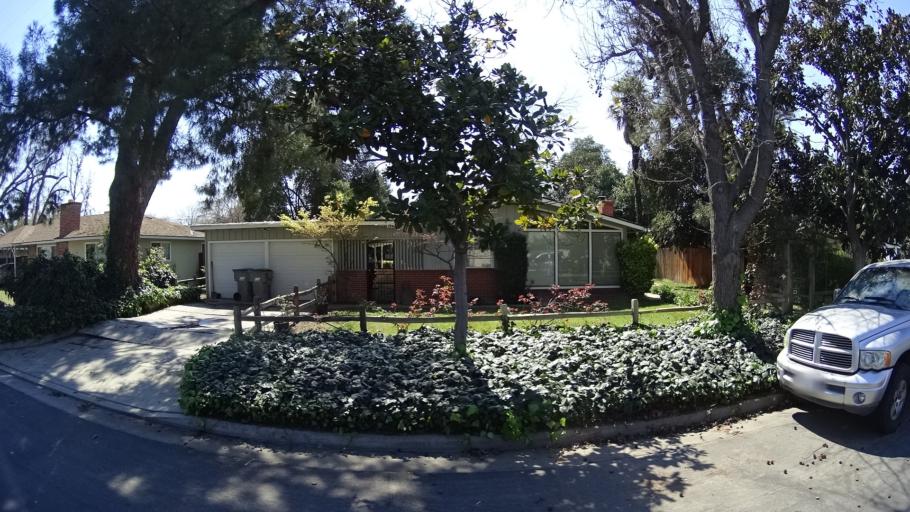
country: US
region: California
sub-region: Fresno County
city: Fresno
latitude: 36.7976
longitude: -119.7947
